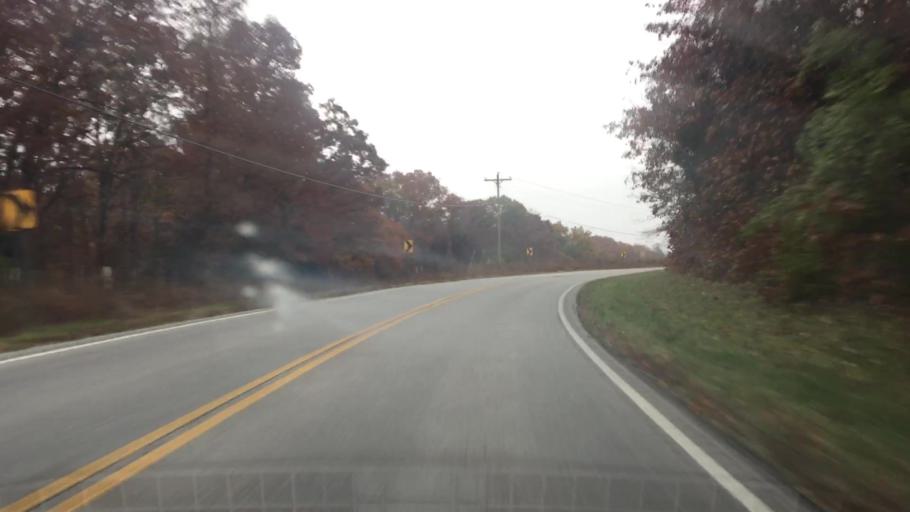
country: US
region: Missouri
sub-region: Callaway County
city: Fulton
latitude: 38.8800
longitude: -92.0863
